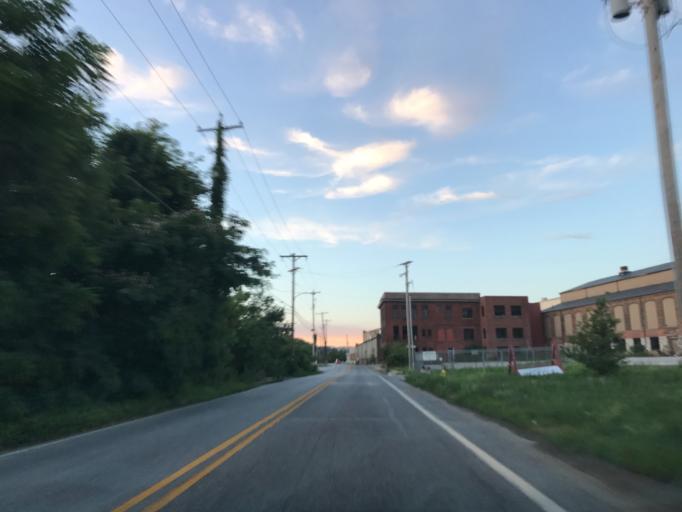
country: US
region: Pennsylvania
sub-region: York County
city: York
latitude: 39.9711
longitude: -76.7247
